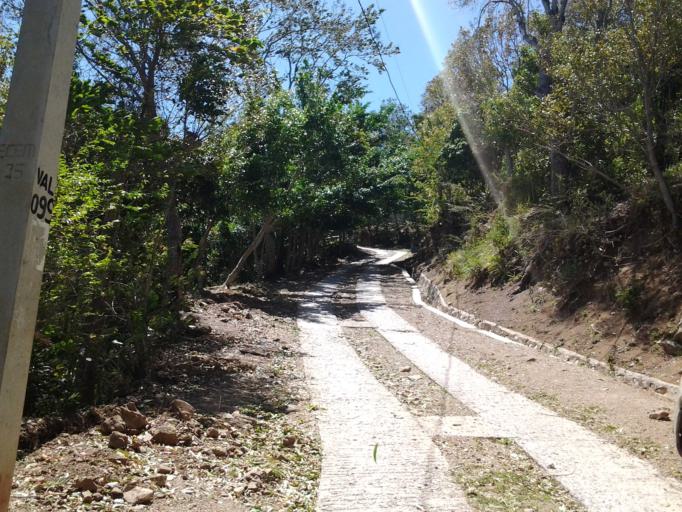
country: HT
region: Ouest
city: Grangwav
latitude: 18.3957
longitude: -72.8150
